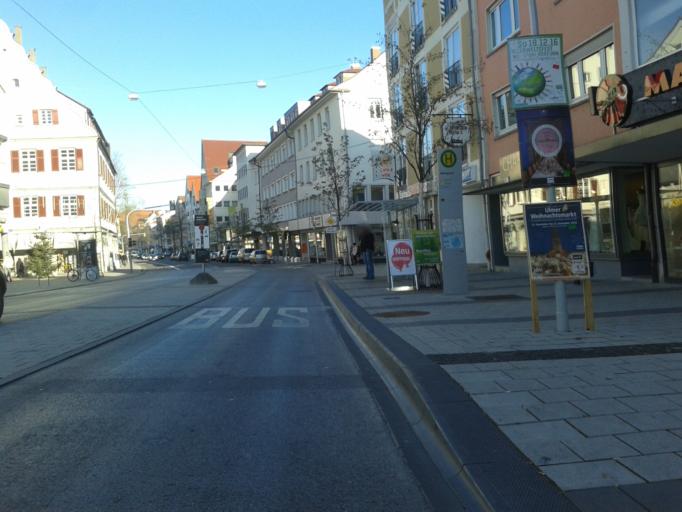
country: DE
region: Baden-Wuerttemberg
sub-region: Tuebingen Region
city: Ulm
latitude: 48.3984
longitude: 9.9962
